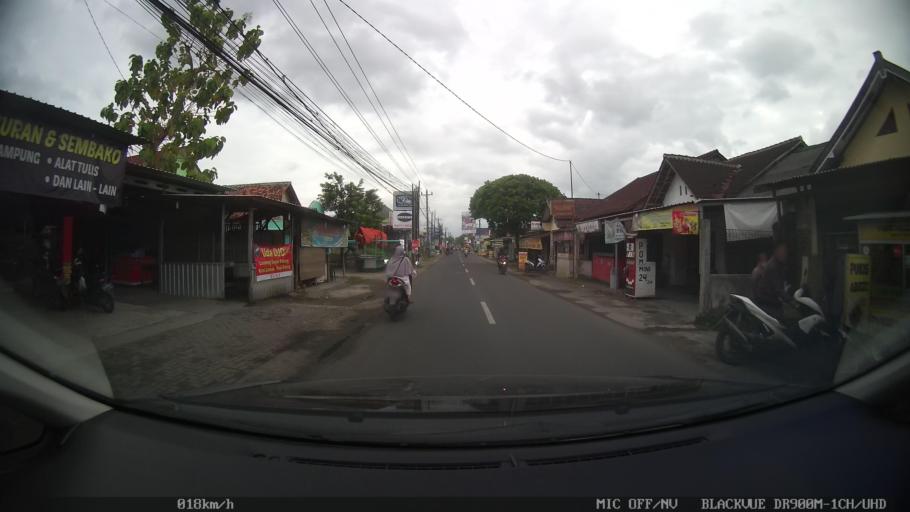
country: ID
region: Daerah Istimewa Yogyakarta
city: Sewon
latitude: -7.8425
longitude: 110.4111
